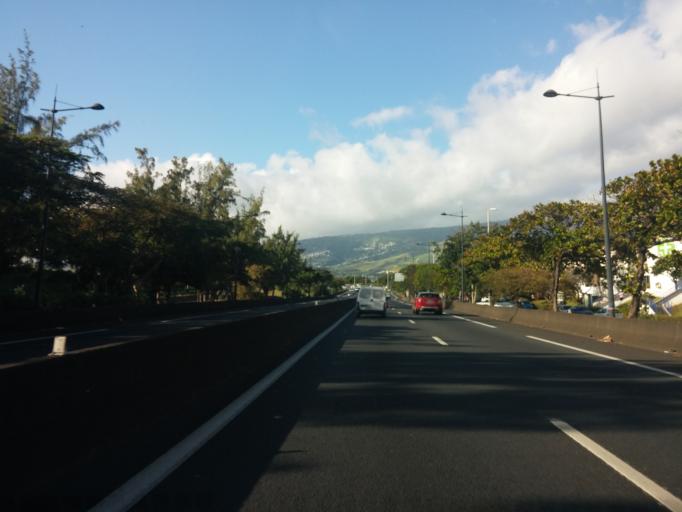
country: RE
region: Reunion
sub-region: Reunion
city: Sainte-Marie
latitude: -20.8900
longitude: 55.5008
